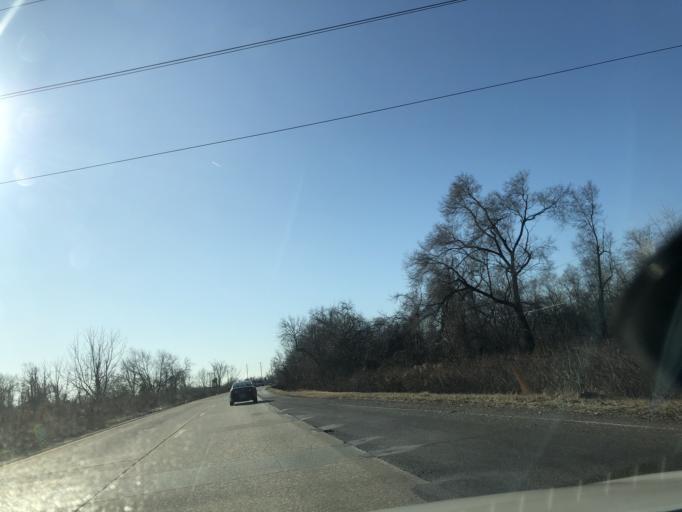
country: US
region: Pennsylvania
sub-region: Bucks County
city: Tullytown
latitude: 40.1481
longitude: -74.8140
